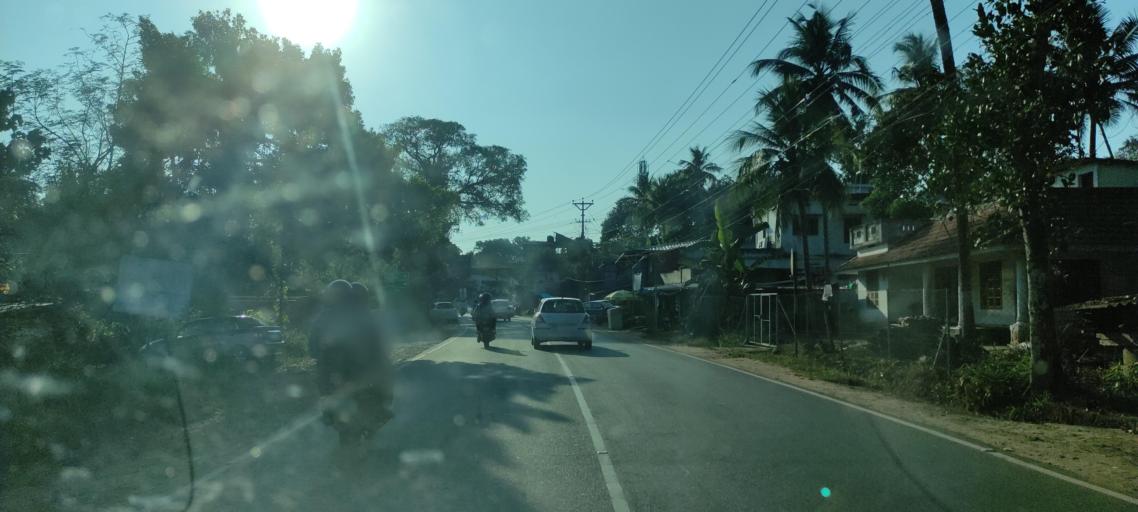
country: IN
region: Kerala
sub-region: Pattanamtitta
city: Adur
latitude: 9.1655
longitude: 76.6864
